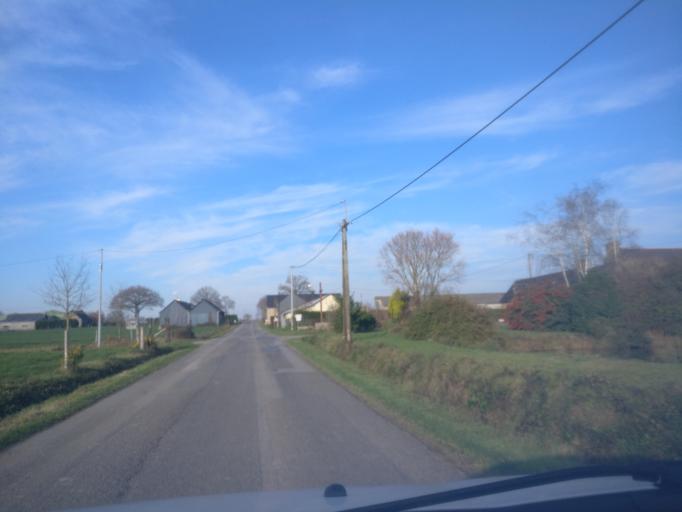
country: FR
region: Brittany
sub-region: Departement d'Ille-et-Vilaine
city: Livre-sur-Changeon
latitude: 48.2035
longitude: -1.3101
